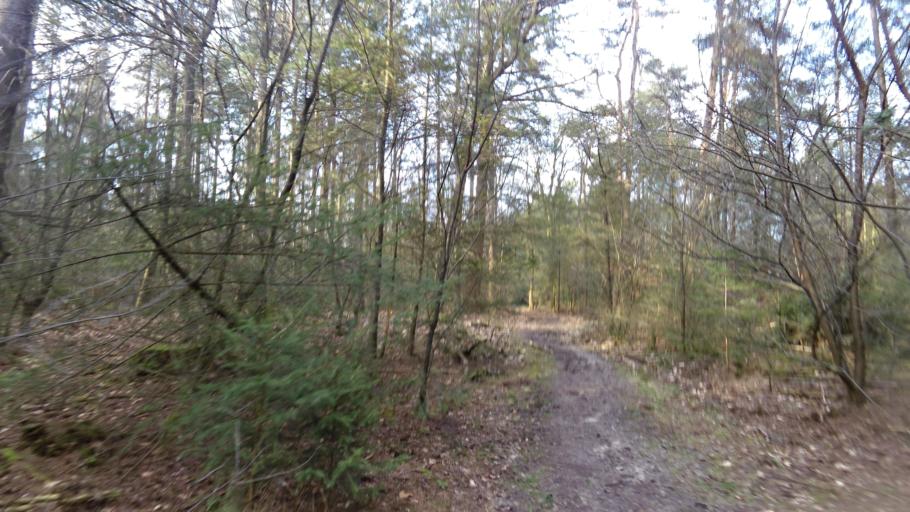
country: NL
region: Gelderland
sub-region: Gemeente Ede
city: Wekerom
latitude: 52.0801
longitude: 5.7245
